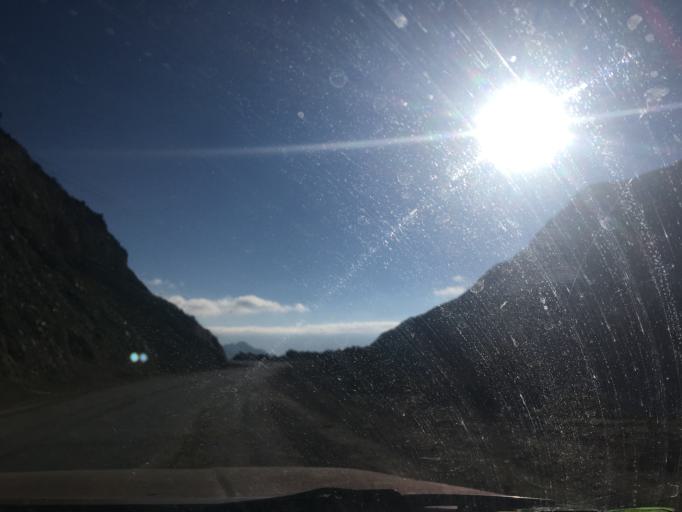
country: BO
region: La Paz
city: Quime
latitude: -17.0144
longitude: -67.2775
